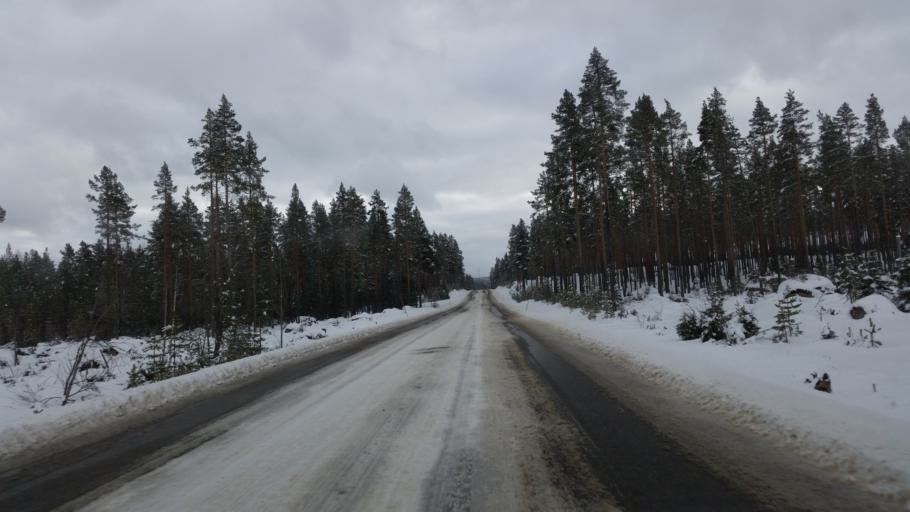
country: SE
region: Gaevleborg
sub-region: Ljusdals Kommun
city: Farila
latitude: 62.0242
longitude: 15.2262
